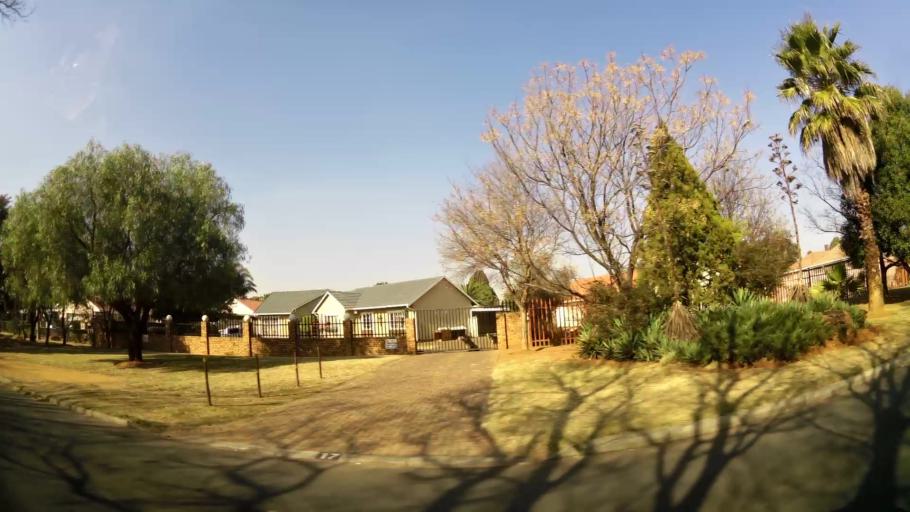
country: ZA
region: Gauteng
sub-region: West Rand District Municipality
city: Randfontein
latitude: -26.1816
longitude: 27.6860
